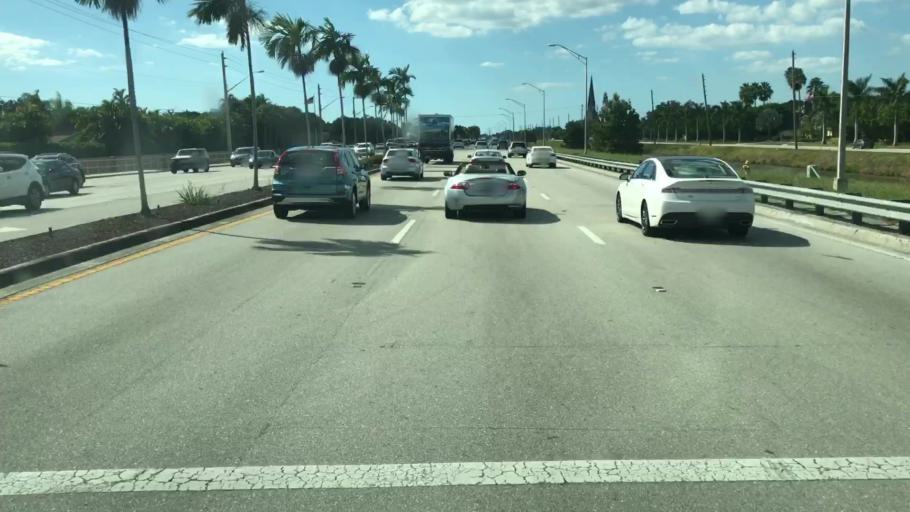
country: US
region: Florida
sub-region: Collier County
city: Naples Park
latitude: 26.2727
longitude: -81.7600
